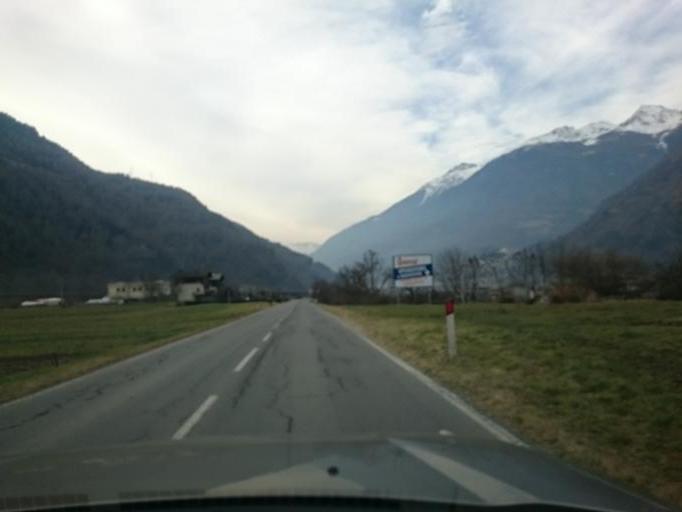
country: IT
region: Lombardy
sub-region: Provincia di Sondrio
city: Grosio
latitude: 46.3087
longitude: 10.2957
